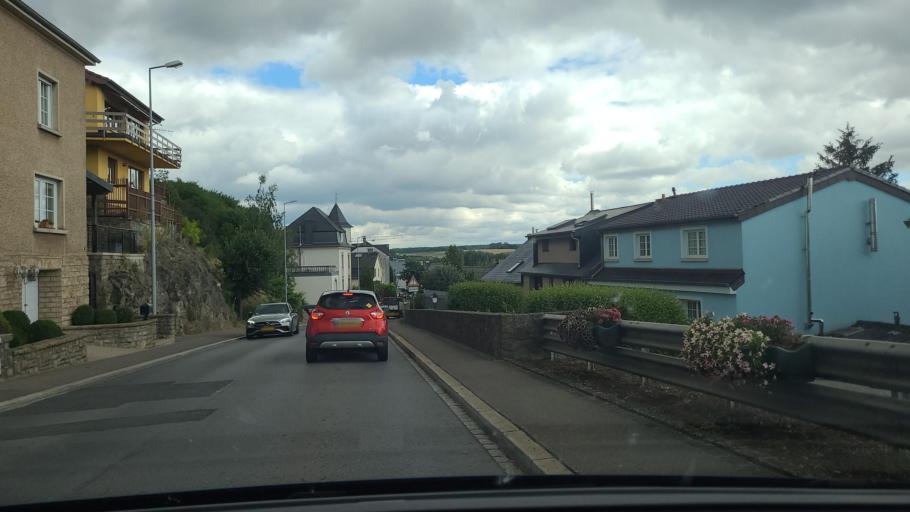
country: LU
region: Luxembourg
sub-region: Canton de Luxembourg
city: Hesperange
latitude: 49.5714
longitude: 6.1503
